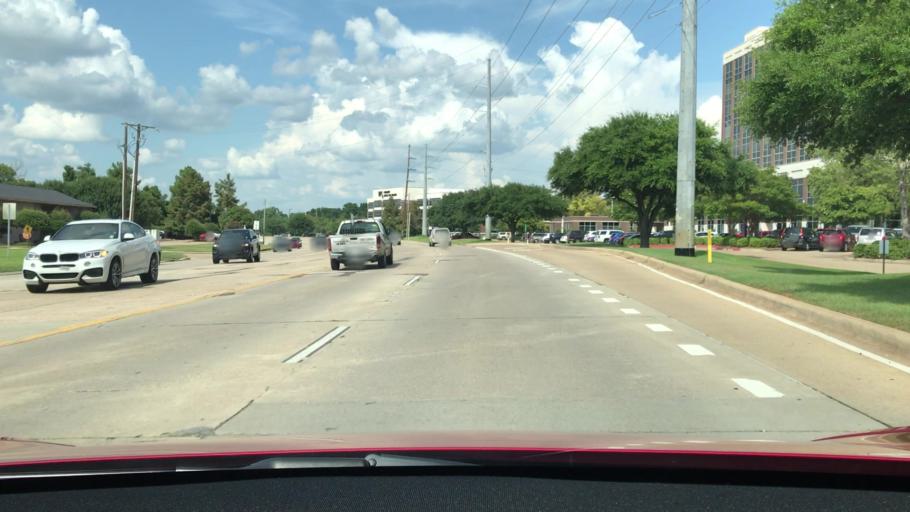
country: US
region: Louisiana
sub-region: Bossier Parish
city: Bossier City
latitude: 32.4322
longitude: -93.7107
